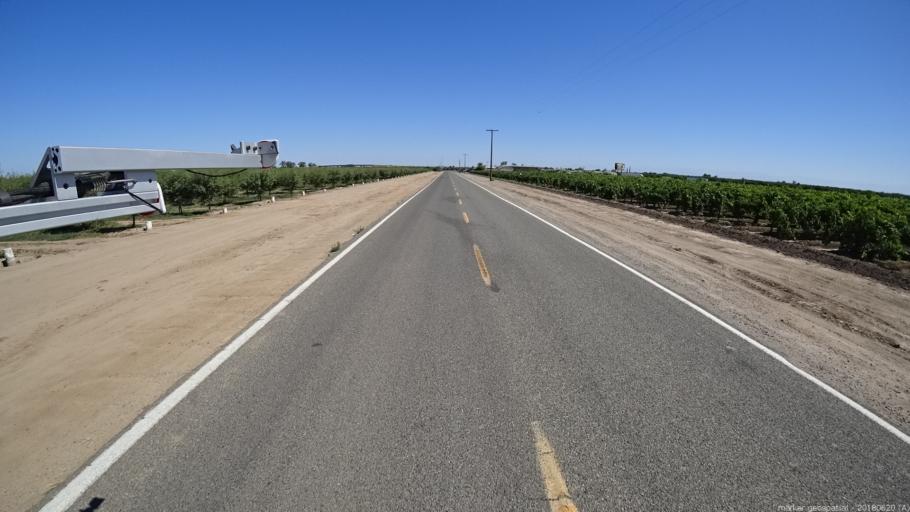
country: US
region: California
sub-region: Madera County
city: Parkwood
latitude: 36.9313
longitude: -120.0334
